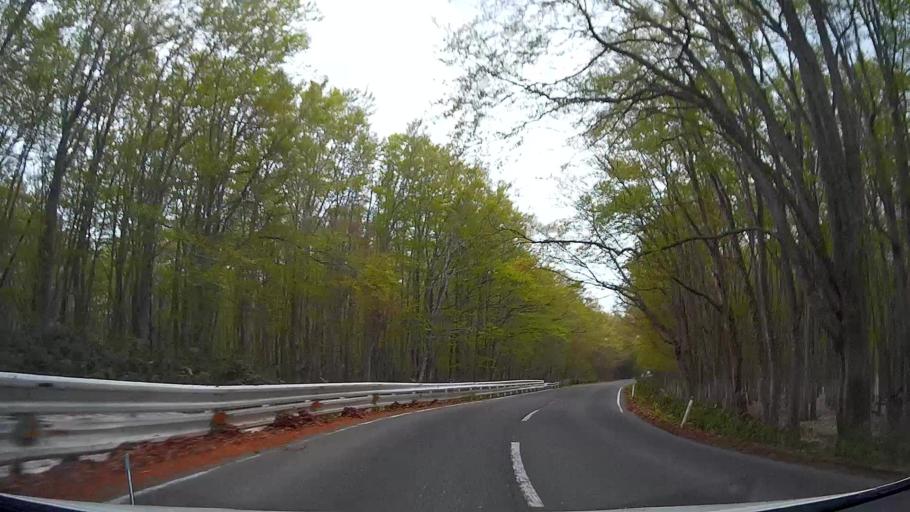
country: JP
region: Aomori
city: Aomori Shi
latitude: 40.6968
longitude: 140.8384
